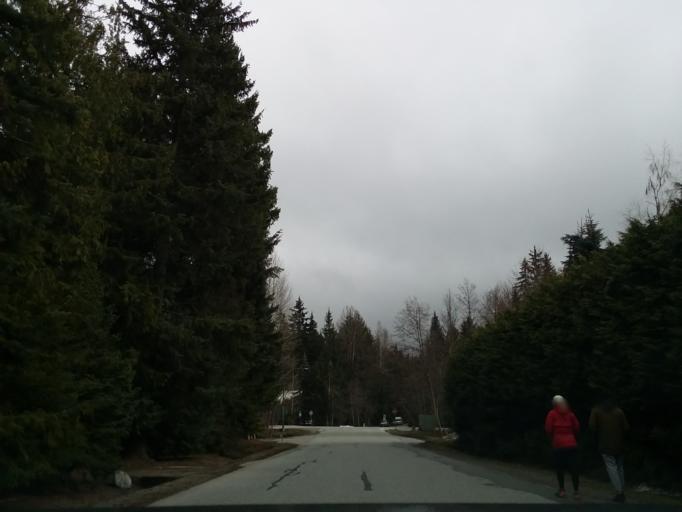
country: CA
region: British Columbia
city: Whistler
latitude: 50.1271
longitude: -122.9679
